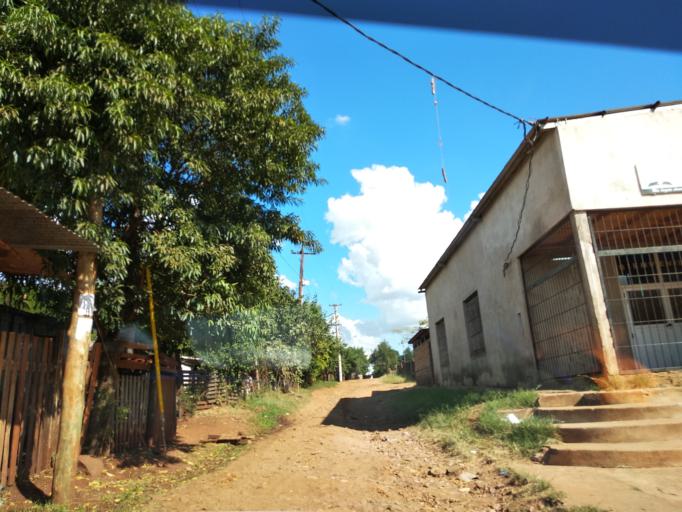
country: AR
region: Misiones
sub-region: Departamento de Capital
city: Posadas
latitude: -27.3894
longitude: -55.9463
